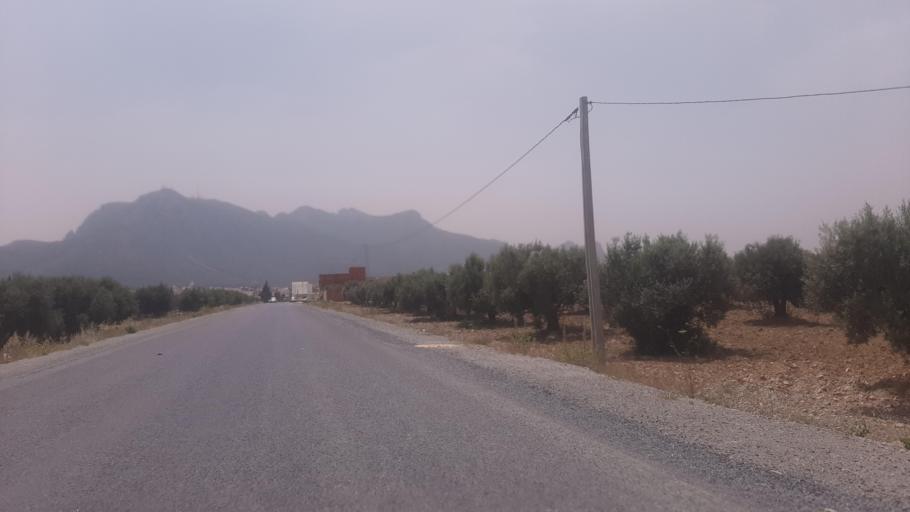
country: TN
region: Zaghwan
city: Zaghouan
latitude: 36.4192
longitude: 10.1368
